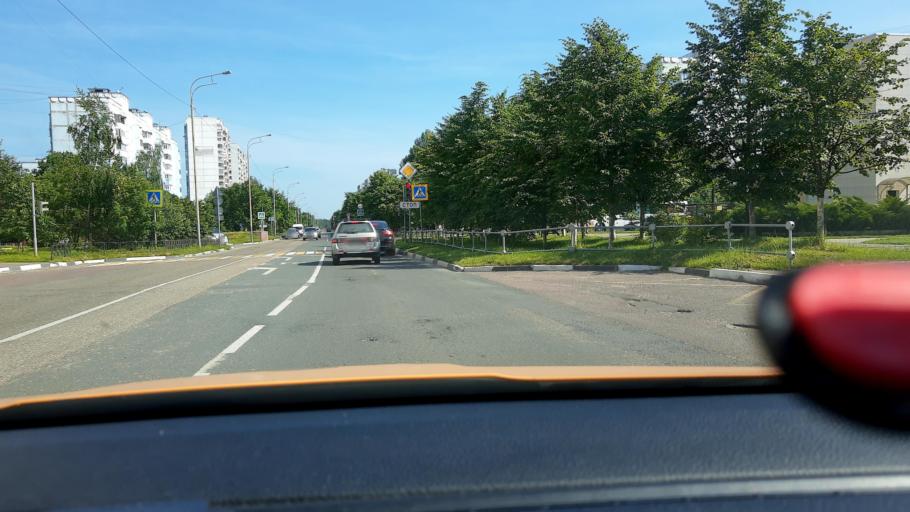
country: RU
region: Moskovskaya
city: Krasnoznamensk
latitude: 55.5921
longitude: 37.0353
